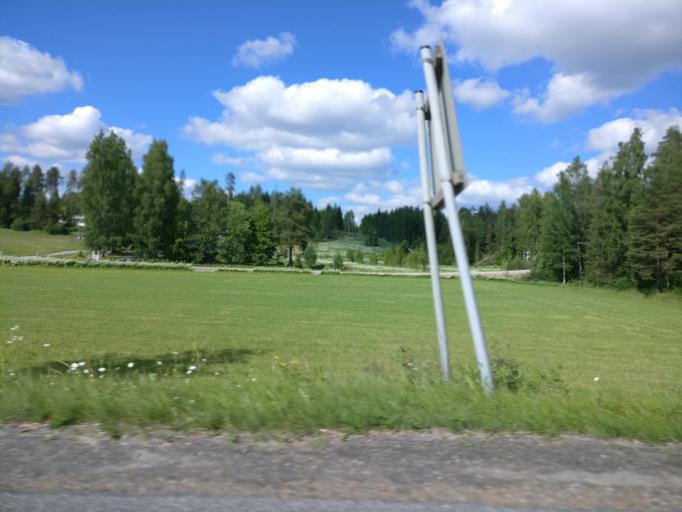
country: FI
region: Southern Savonia
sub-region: Savonlinna
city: Kerimaeki
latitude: 61.8836
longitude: 29.0998
